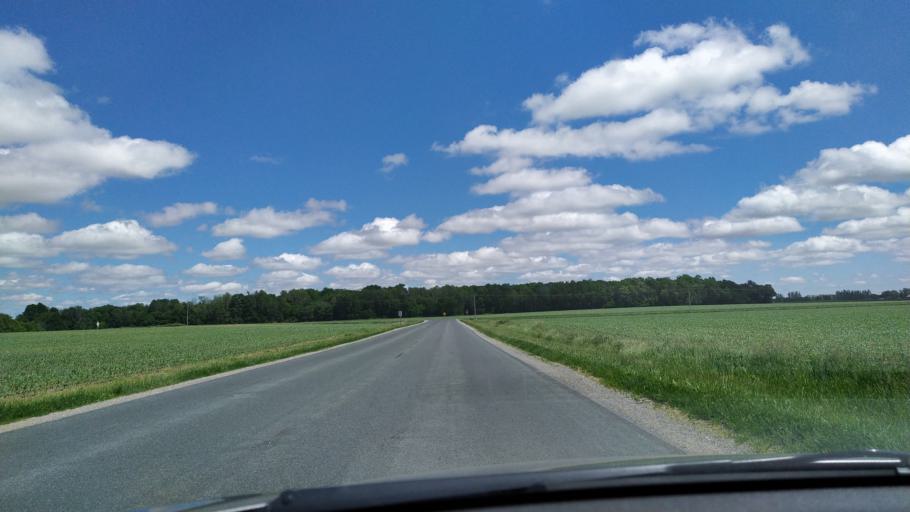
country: CA
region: Ontario
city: Huron East
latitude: 43.4518
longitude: -81.1851
